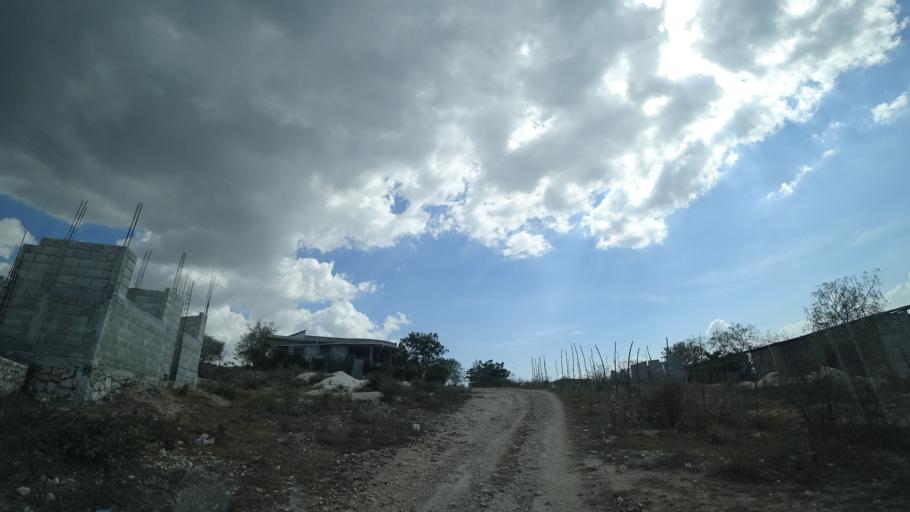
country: HT
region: Ouest
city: Cabaret
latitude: 18.6784
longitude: -72.3178
